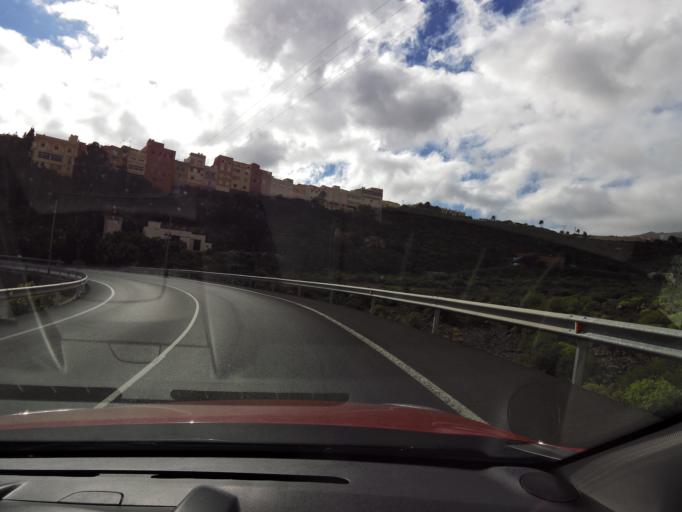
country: ES
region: Canary Islands
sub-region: Provincia de Las Palmas
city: Aguimes
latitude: 27.9089
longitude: -15.4457
